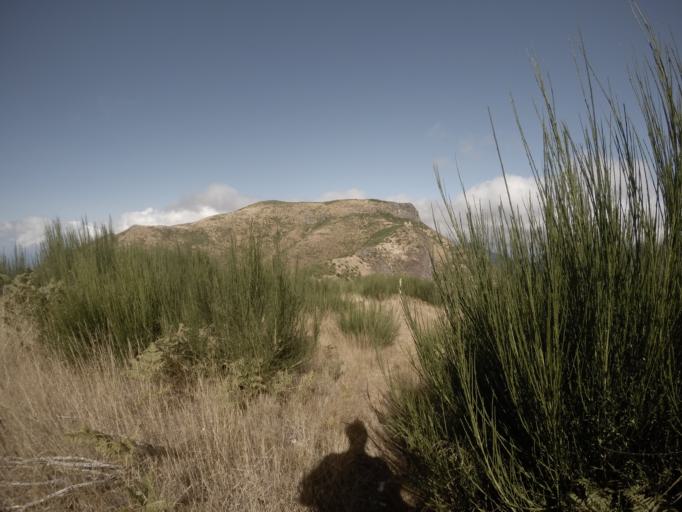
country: PT
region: Madeira
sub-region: Camara de Lobos
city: Curral das Freiras
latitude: 32.7149
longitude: -16.9962
